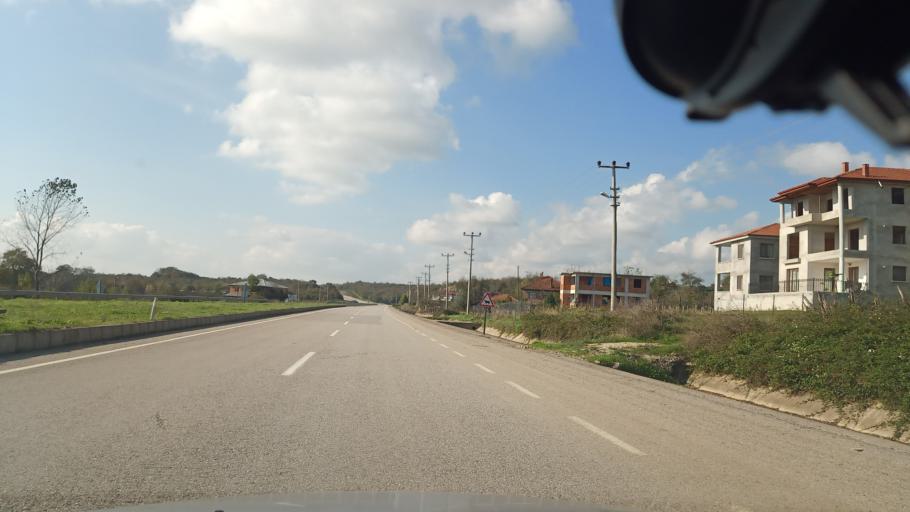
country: TR
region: Sakarya
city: Kaynarca
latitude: 41.0716
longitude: 30.3739
